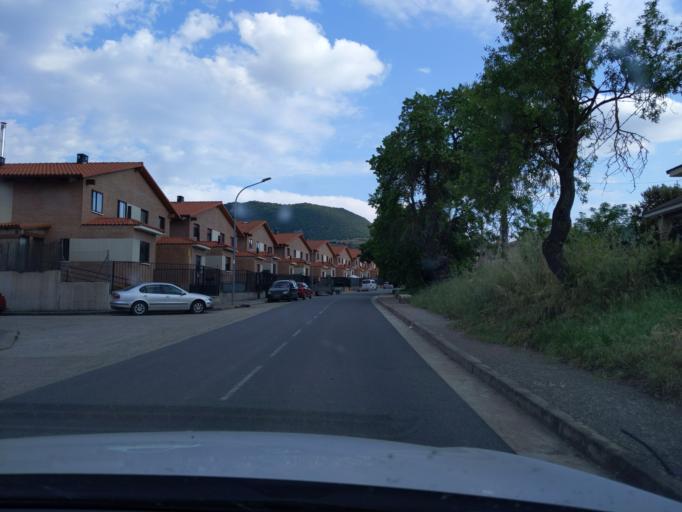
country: ES
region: La Rioja
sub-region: Provincia de La Rioja
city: Clavijo
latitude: 42.3716
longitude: -2.4228
